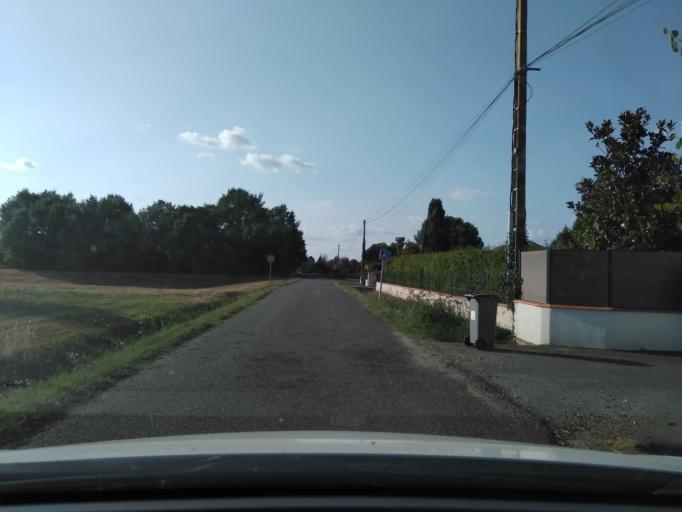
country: FR
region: Midi-Pyrenees
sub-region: Departement du Tarn-et-Garonne
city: Montech
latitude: 43.9659
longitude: 1.2463
